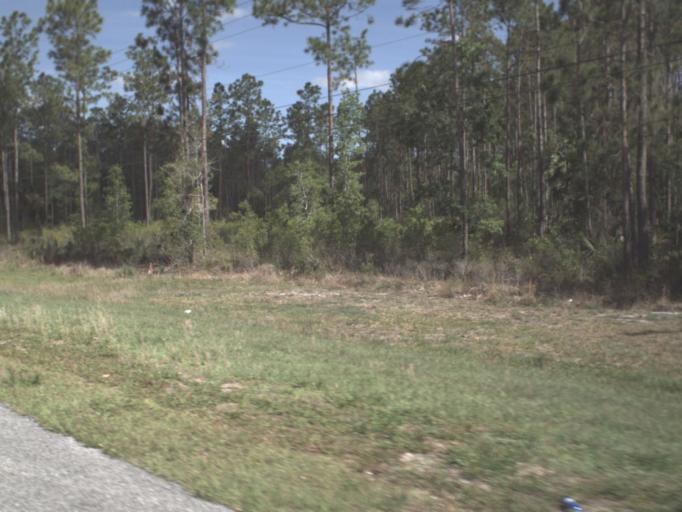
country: US
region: Florida
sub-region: Flagler County
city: Bunnell
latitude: 29.4223
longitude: -81.2149
